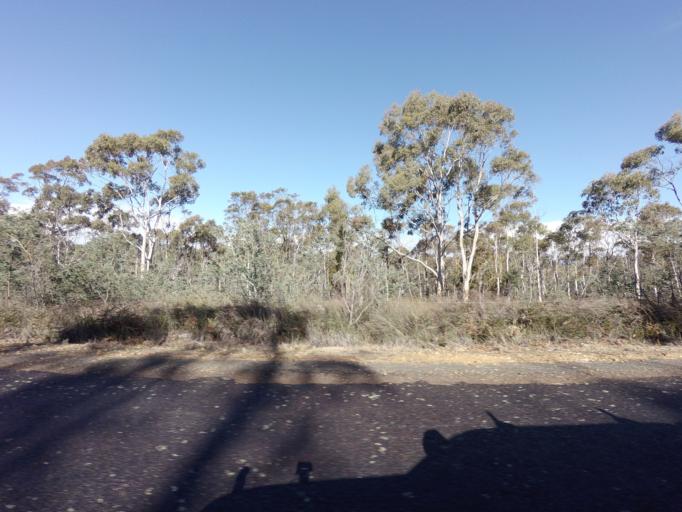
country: AU
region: Tasmania
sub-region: Sorell
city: Sorell
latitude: -42.3619
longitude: 147.9538
